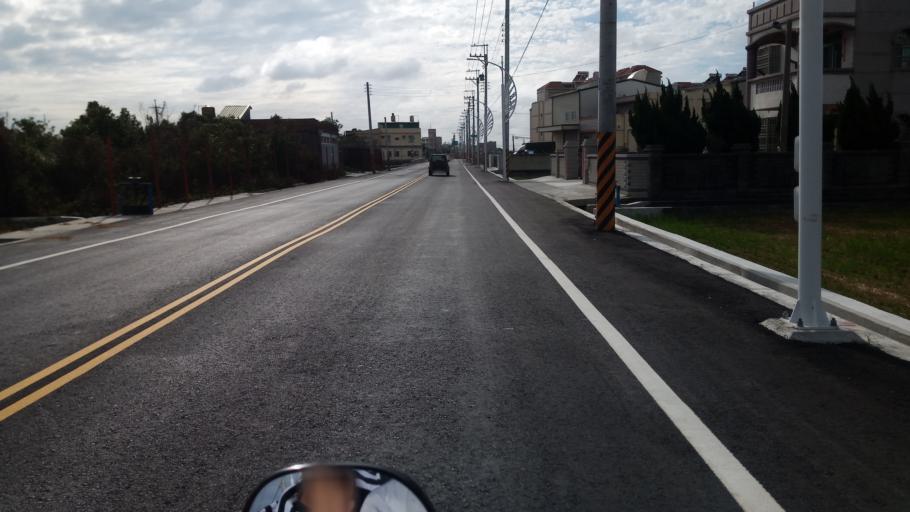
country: TW
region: Taiwan
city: Fengyuan
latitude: 24.4207
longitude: 120.6580
